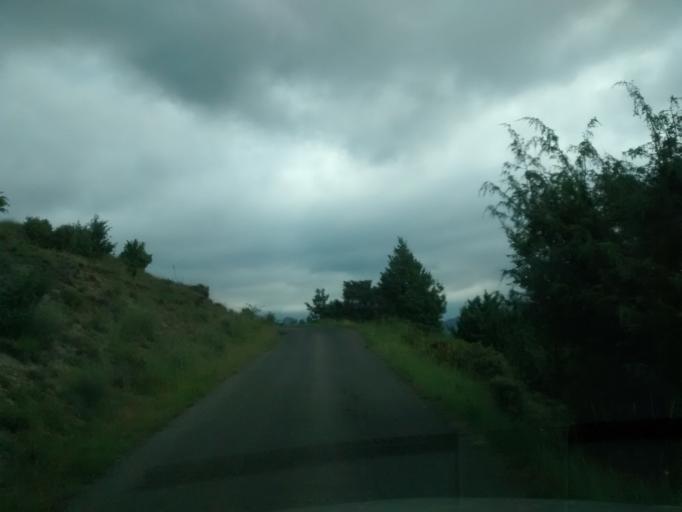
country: ES
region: Aragon
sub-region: Provincia de Huesca
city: Puertolas
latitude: 42.5543
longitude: 0.1376
